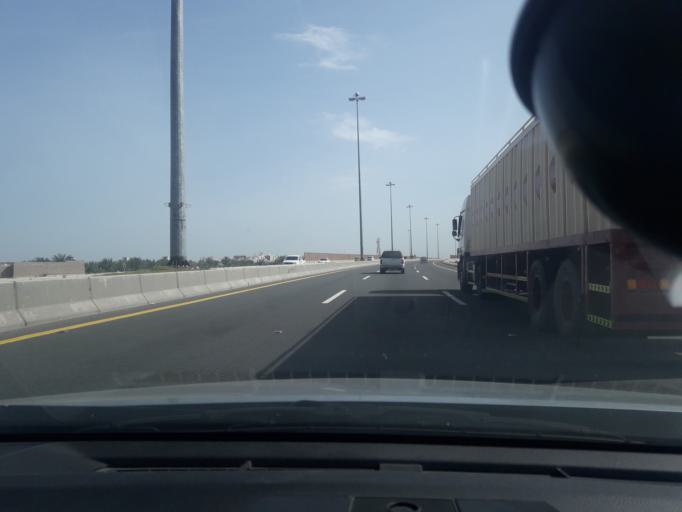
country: SA
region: Al Madinah al Munawwarah
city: Medina
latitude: 24.4436
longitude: 39.6368
